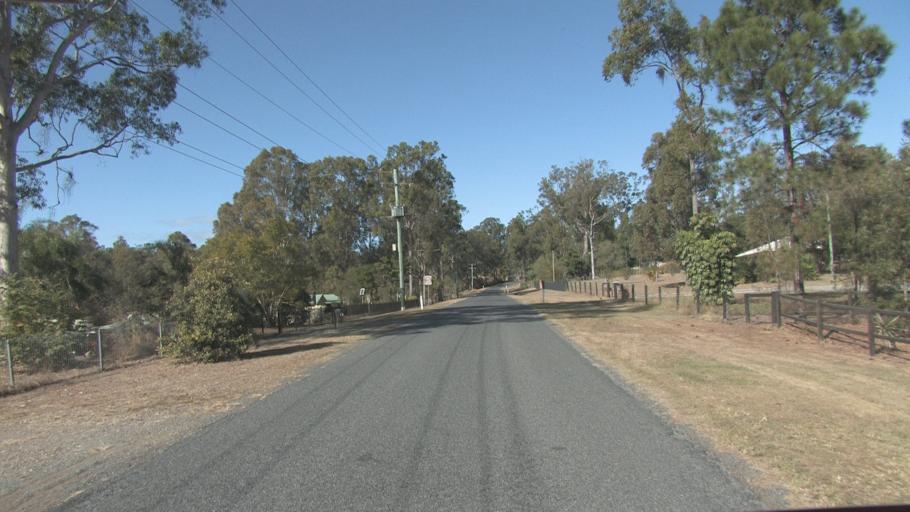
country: AU
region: Queensland
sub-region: Logan
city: Cedar Vale
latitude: -27.8741
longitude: 152.9844
